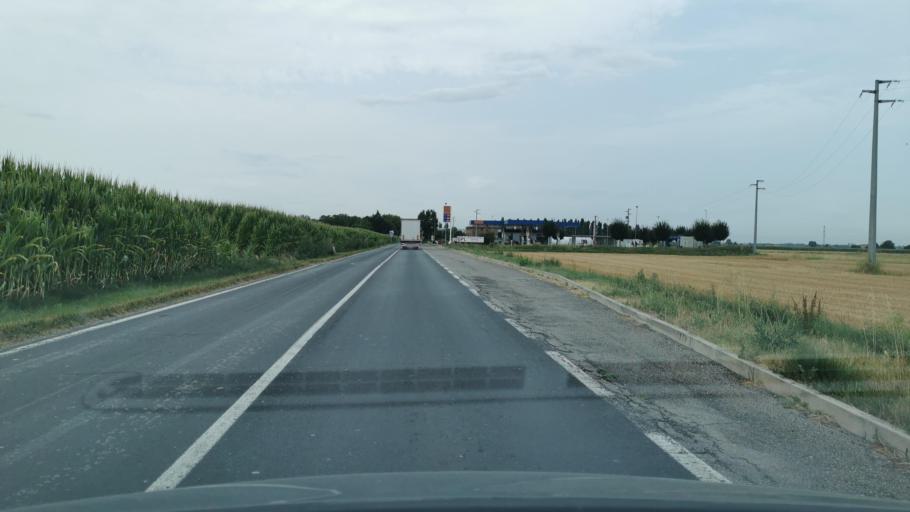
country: IT
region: Emilia-Romagna
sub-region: Provincia di Modena
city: Villanova
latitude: 44.7038
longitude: 10.8965
